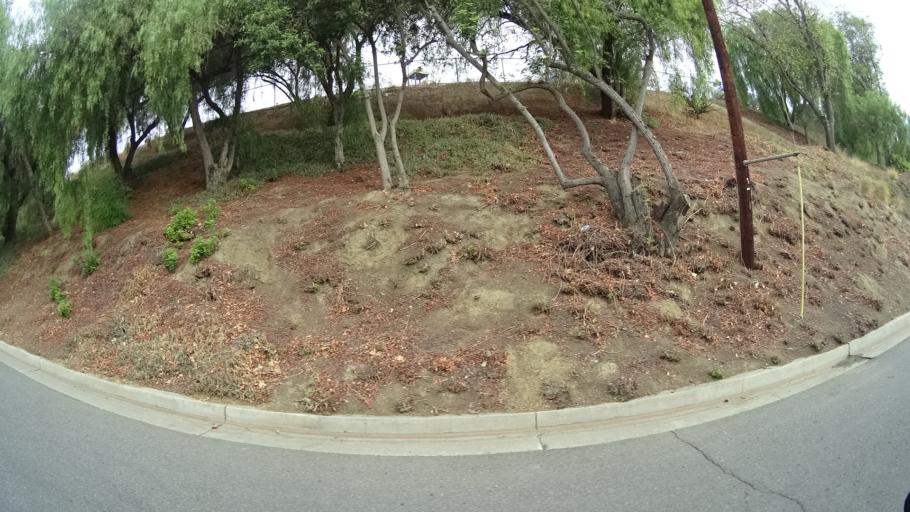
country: US
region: California
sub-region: Orange County
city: Villa Park
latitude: 33.8363
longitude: -117.8275
